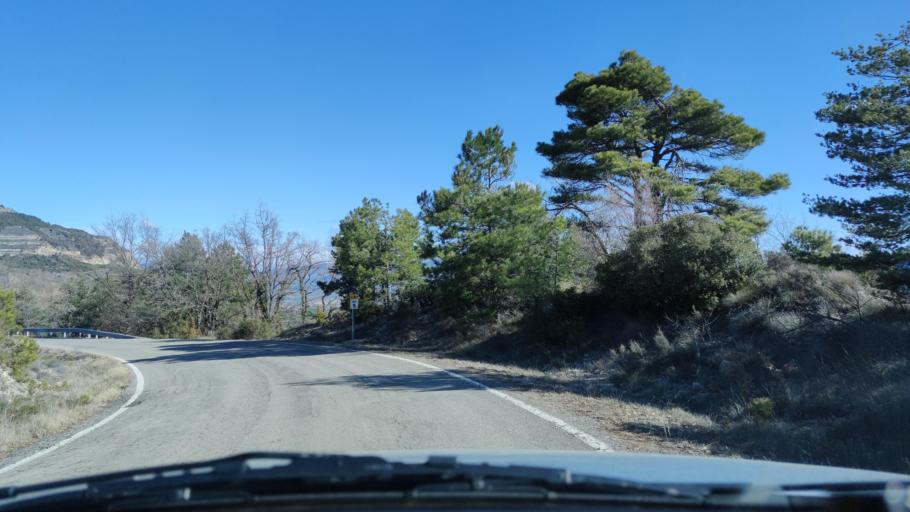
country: ES
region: Catalonia
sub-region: Provincia de Lleida
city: Llimiana
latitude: 42.0434
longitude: 1.0459
